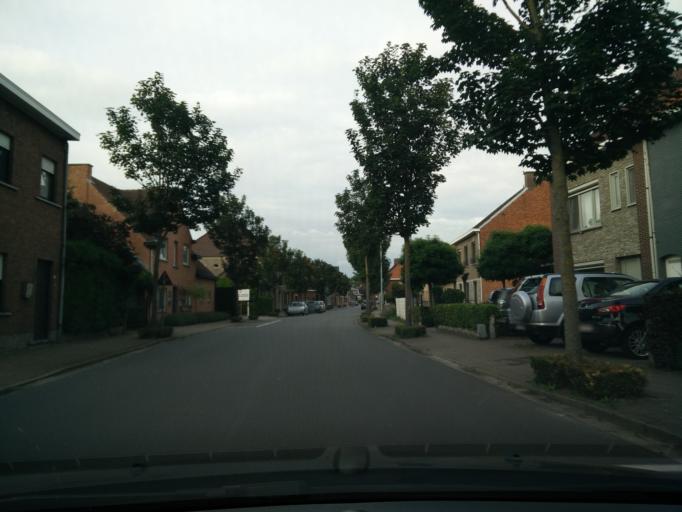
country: BE
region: Flanders
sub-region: Provincie Antwerpen
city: Bornem
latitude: 51.0939
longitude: 4.2363
